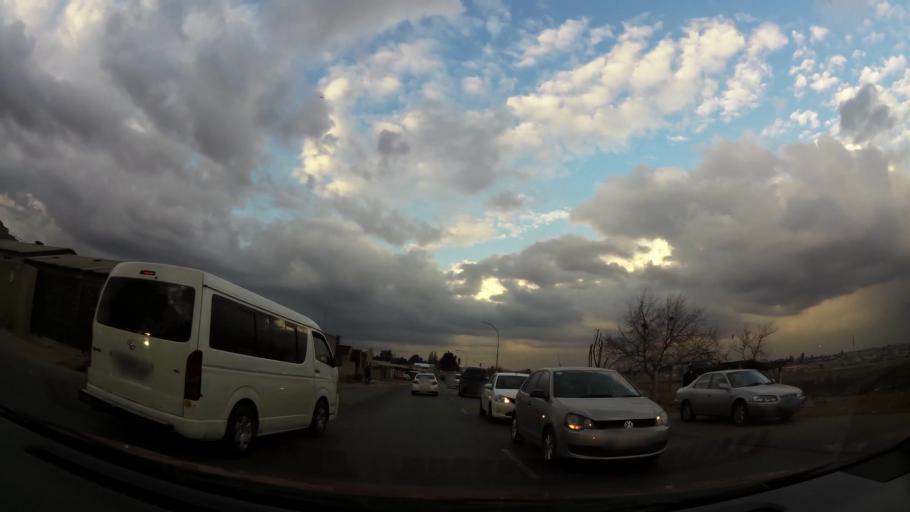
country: ZA
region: Gauteng
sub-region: City of Johannesburg Metropolitan Municipality
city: Soweto
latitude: -26.2412
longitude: 27.8405
